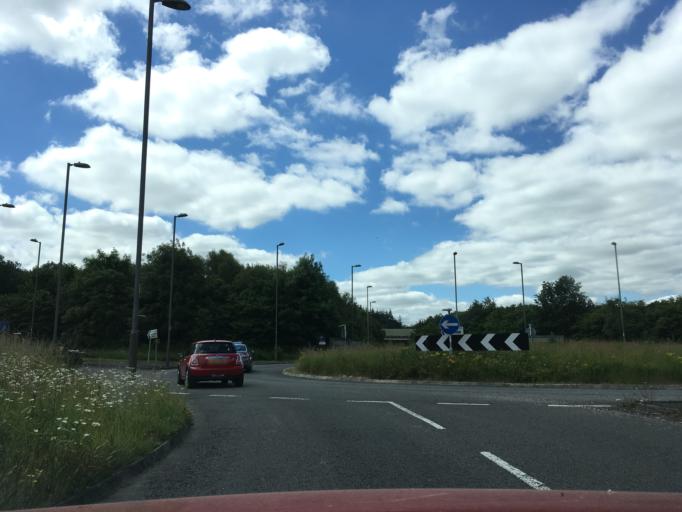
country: GB
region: England
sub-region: Hampshire
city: Highclere
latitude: 51.3641
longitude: -1.3555
